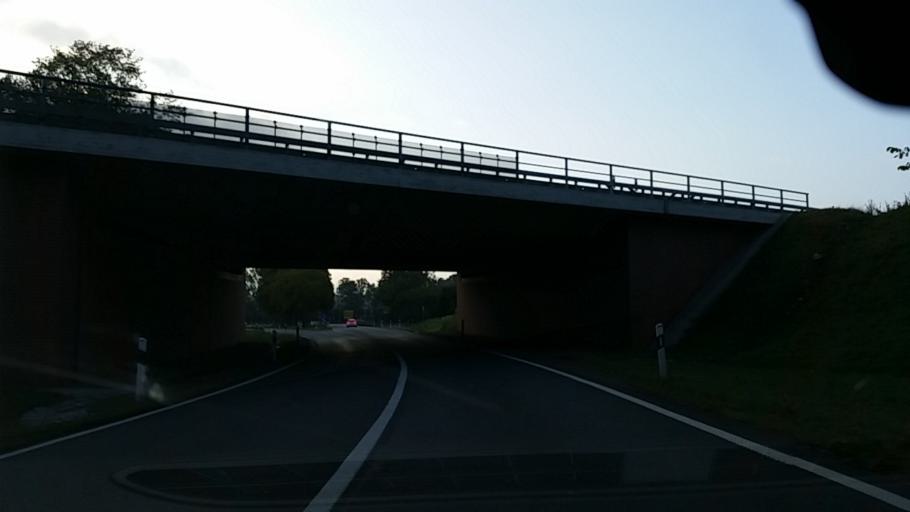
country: DE
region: Lower Saxony
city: Seesen
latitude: 51.8840
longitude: 10.1291
